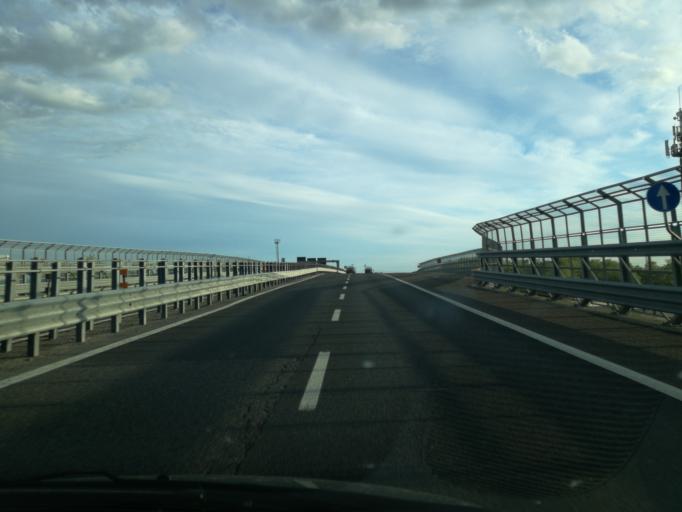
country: IT
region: Lombardy
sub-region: Provincia di Monza e Brianza
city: Agrate Brianza
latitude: 45.5671
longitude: 9.3364
